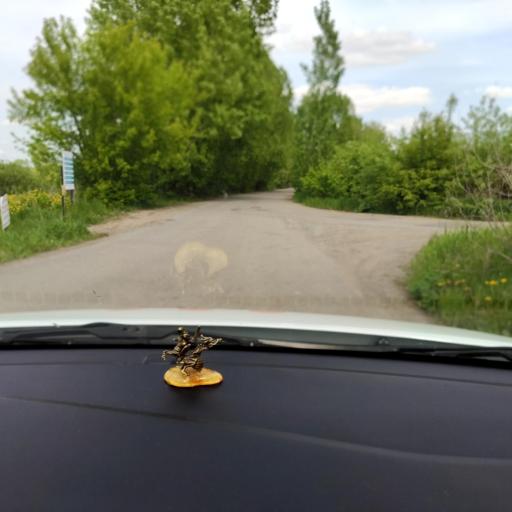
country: RU
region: Tatarstan
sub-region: Gorod Kazan'
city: Kazan
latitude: 55.7003
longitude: 49.0637
